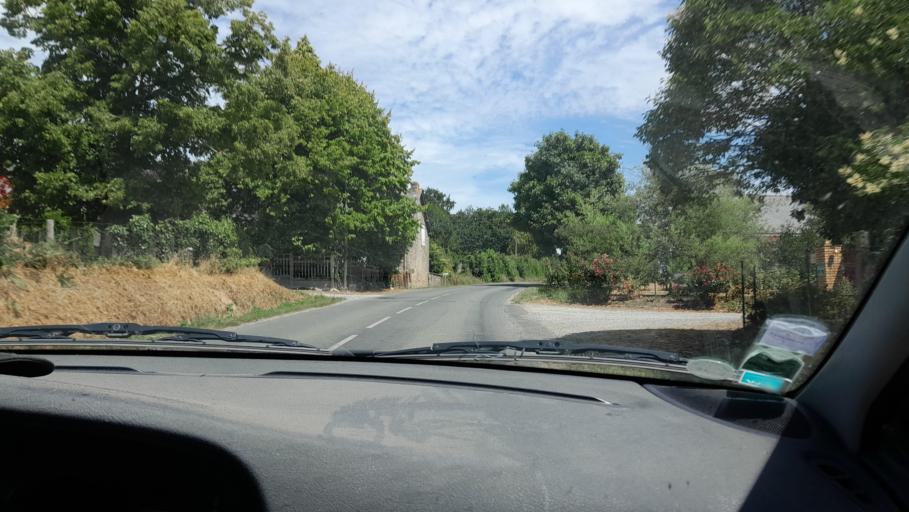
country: FR
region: Brittany
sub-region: Departement d'Ille-et-Vilaine
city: Le Pertre
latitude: 48.0651
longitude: -1.0271
